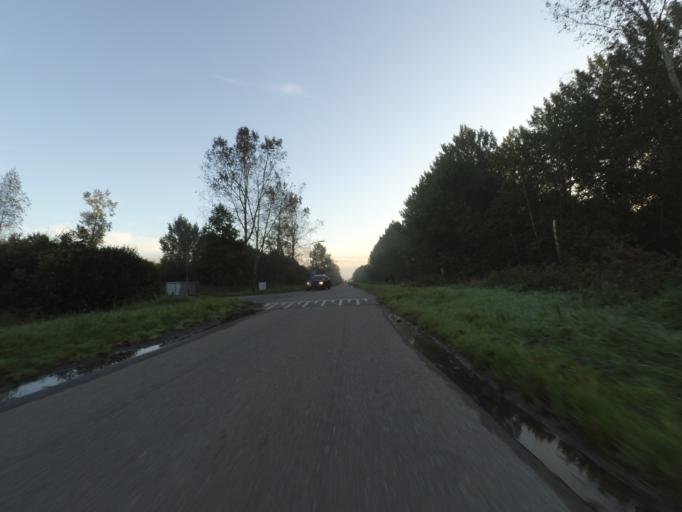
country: NL
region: Flevoland
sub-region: Gemeente Zeewolde
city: Zeewolde
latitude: 52.3416
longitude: 5.4721
